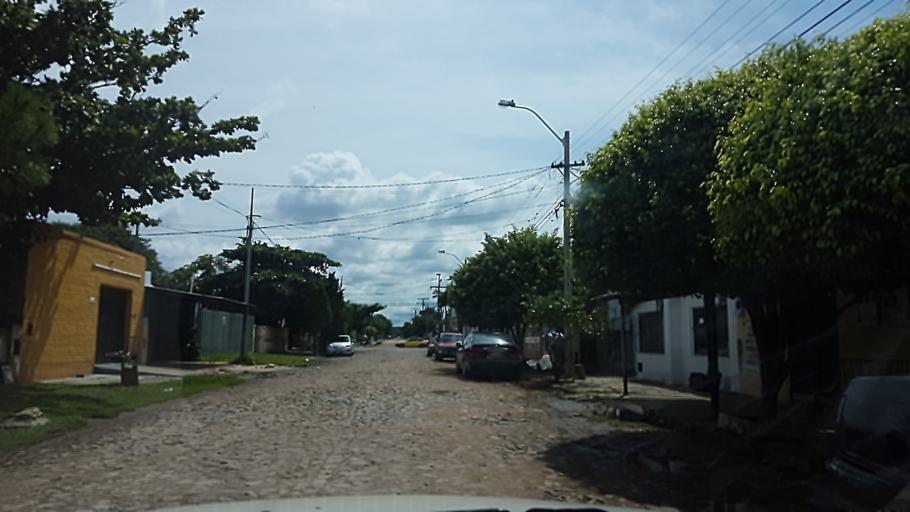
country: PY
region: Central
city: Colonia Mariano Roque Alonso
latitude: -25.2095
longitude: -57.5326
